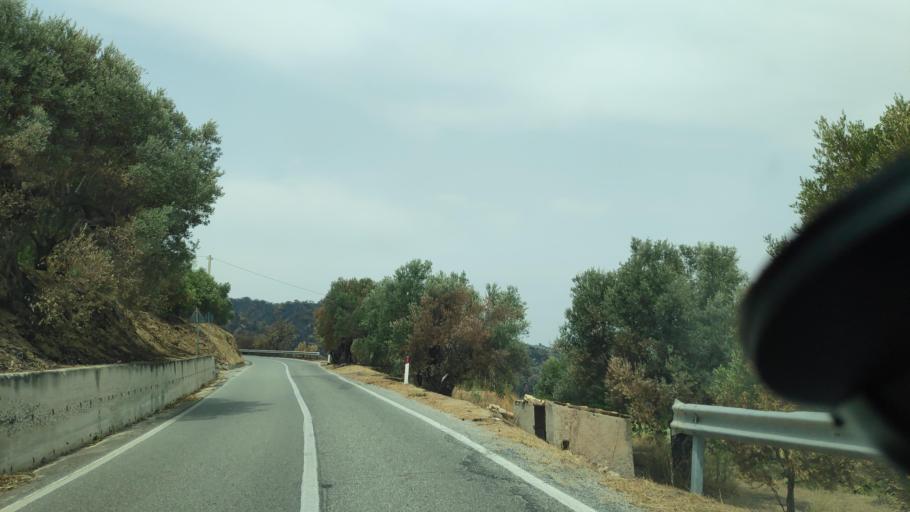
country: IT
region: Calabria
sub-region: Provincia di Catanzaro
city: Sant'Andrea Apostolo dello Ionio
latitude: 38.6457
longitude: 16.5306
